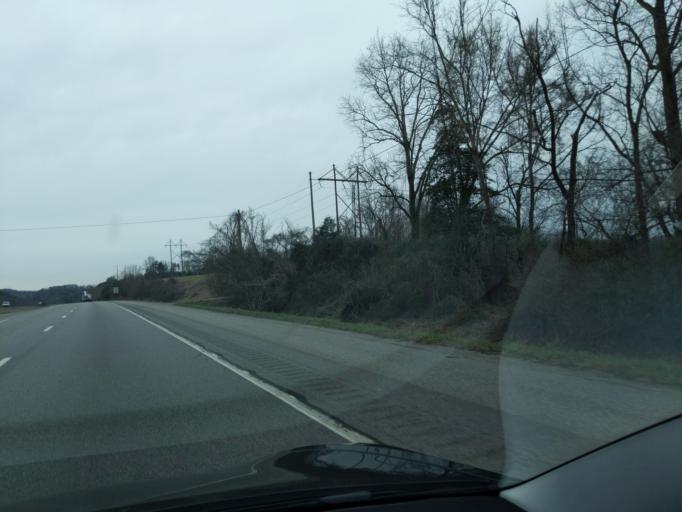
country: US
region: Kentucky
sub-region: Knox County
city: Barbourville
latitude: 36.8525
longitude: -83.7906
